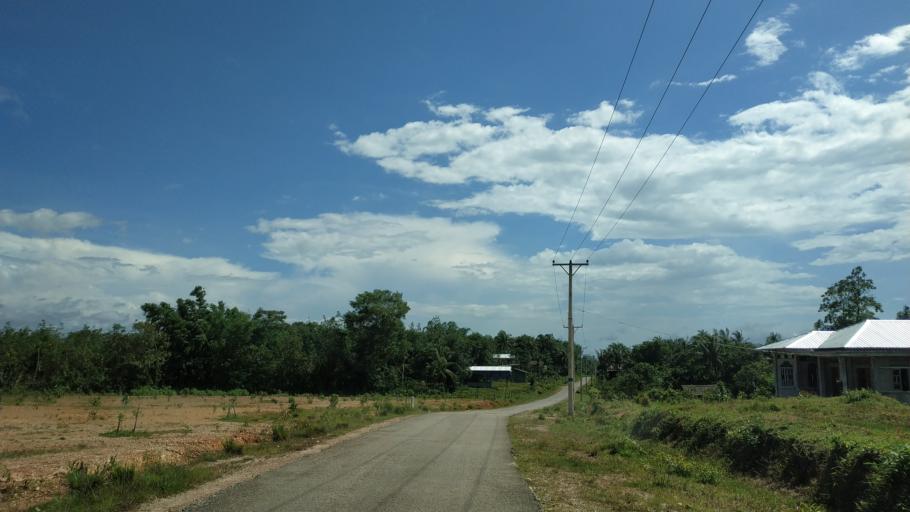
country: MM
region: Tanintharyi
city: Dawei
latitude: 14.2246
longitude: 98.1964
